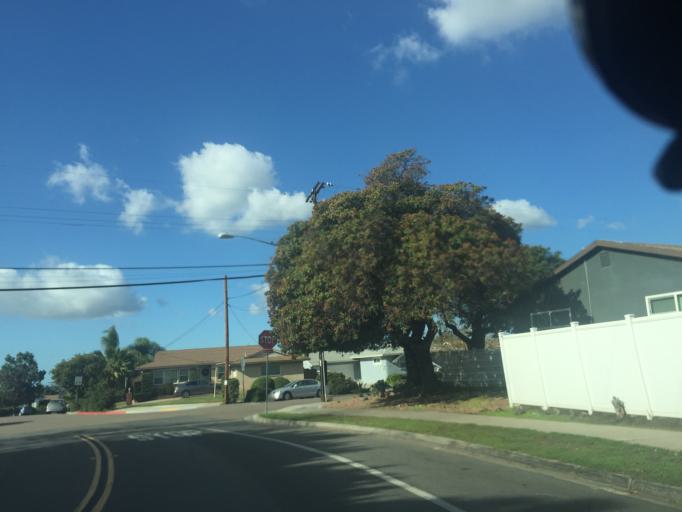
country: US
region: California
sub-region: San Diego County
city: La Mesa
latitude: 32.7959
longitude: -117.0831
